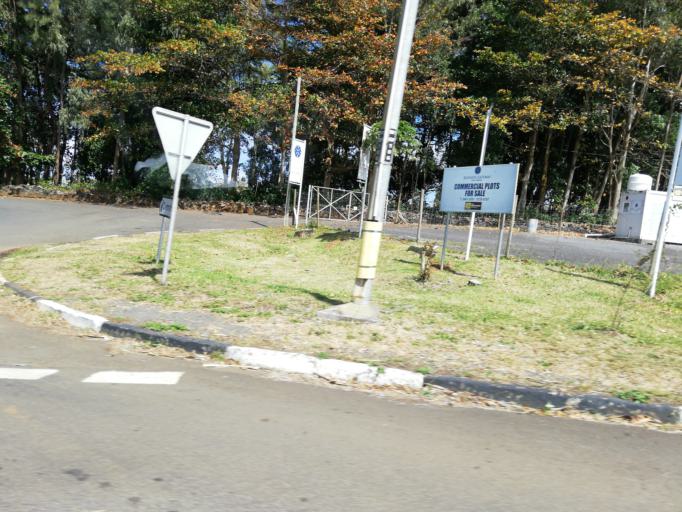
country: MU
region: Grand Port
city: Plaine Magnien
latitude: -20.4241
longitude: 57.6596
